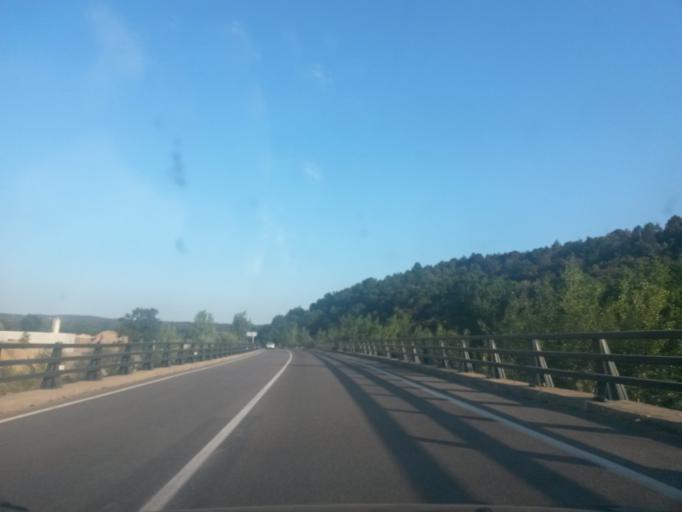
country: ES
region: Catalonia
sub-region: Provincia de Girona
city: Besalu
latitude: 42.1948
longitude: 2.7255
